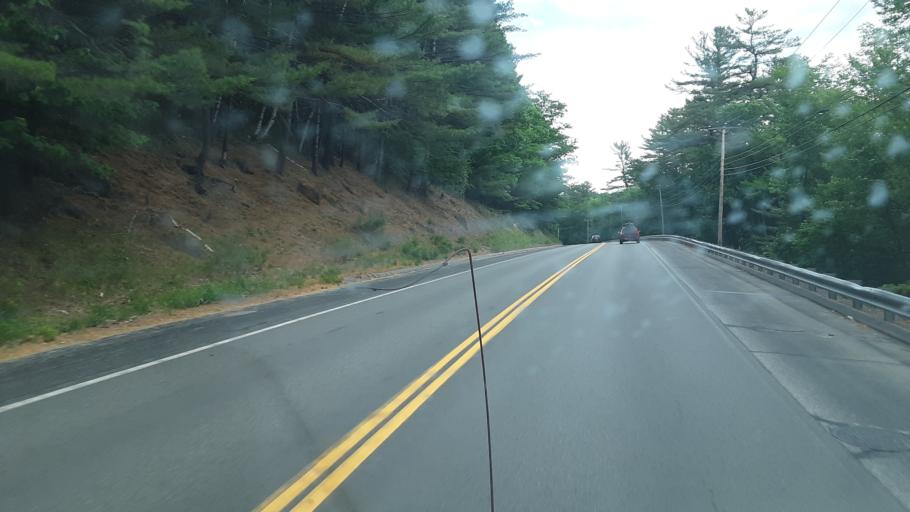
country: US
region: Maine
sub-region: Oxford County
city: Dixfield
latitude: 44.5319
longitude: -70.4920
